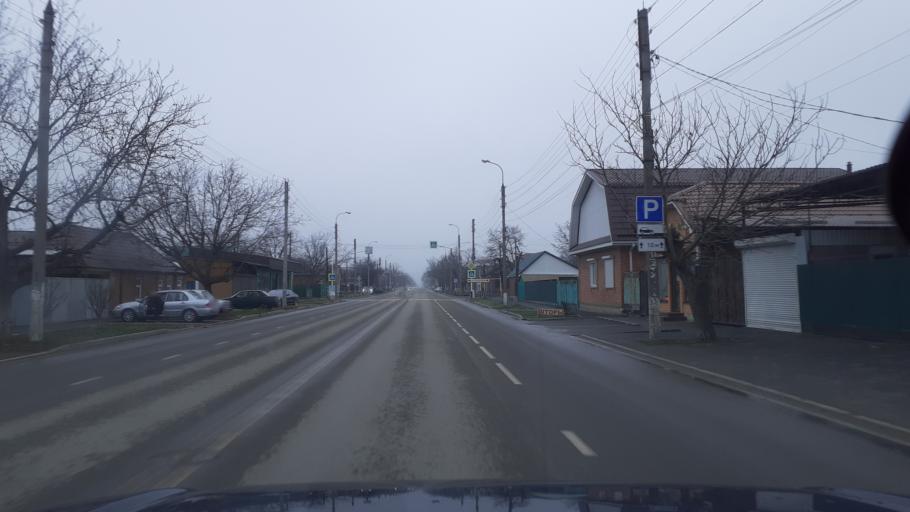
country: RU
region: Adygeya
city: Maykop
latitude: 44.6151
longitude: 40.0815
